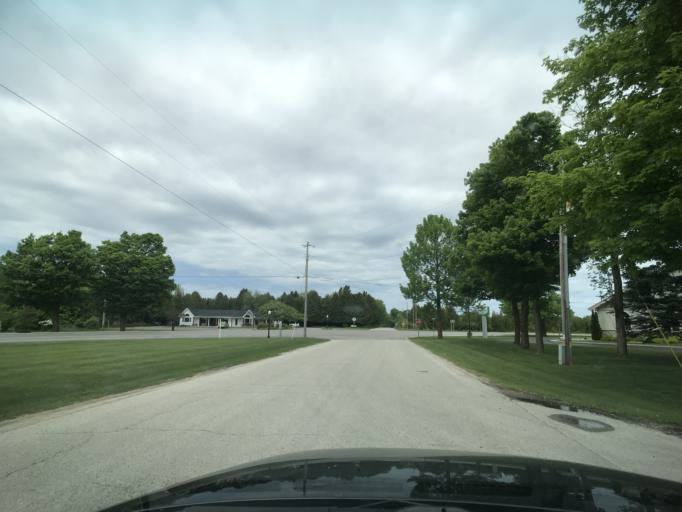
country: US
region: Wisconsin
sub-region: Door County
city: Sturgeon Bay
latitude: 45.1777
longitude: -87.1532
